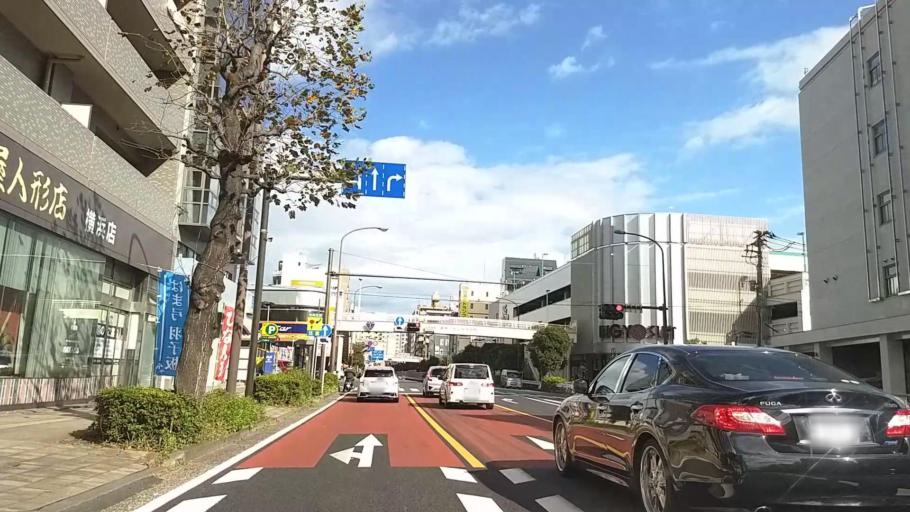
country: JP
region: Kanagawa
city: Yokohama
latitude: 35.4773
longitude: 139.6287
